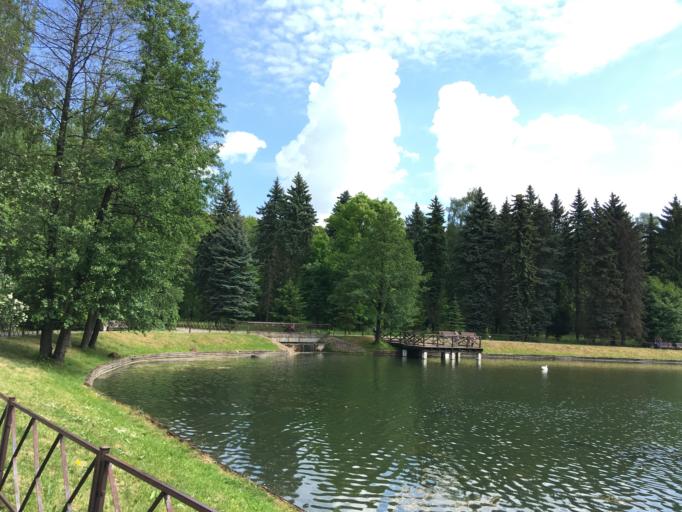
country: BY
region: Minsk
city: Minsk
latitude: 53.9132
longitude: 27.6150
